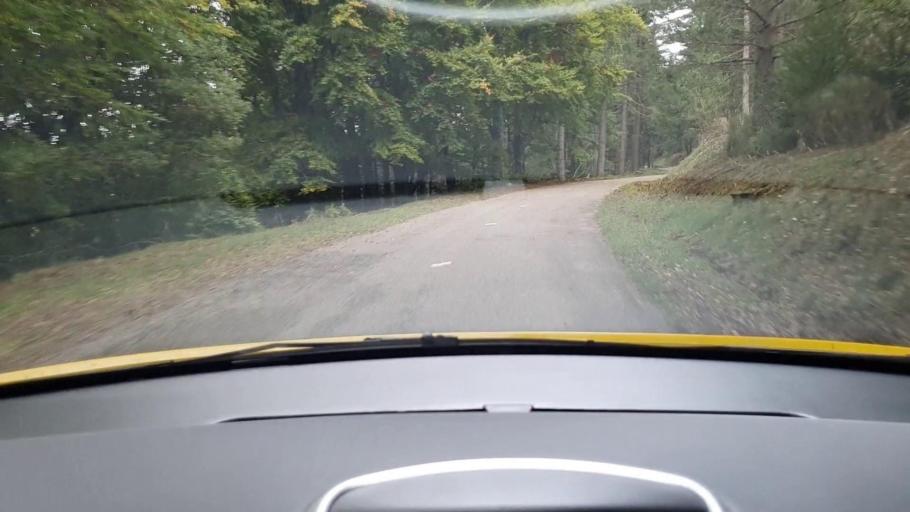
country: FR
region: Languedoc-Roussillon
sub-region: Departement de la Lozere
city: Meyrueis
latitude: 44.0903
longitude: 3.4559
